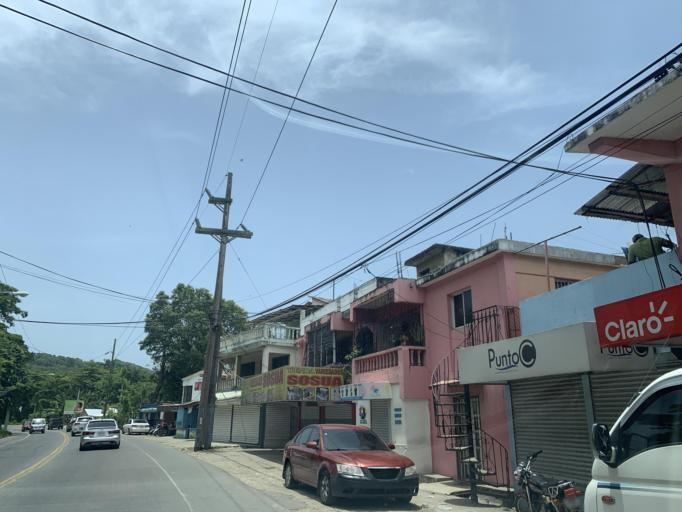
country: DO
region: Puerto Plata
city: Cabarete
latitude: 19.7447
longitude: -70.5218
